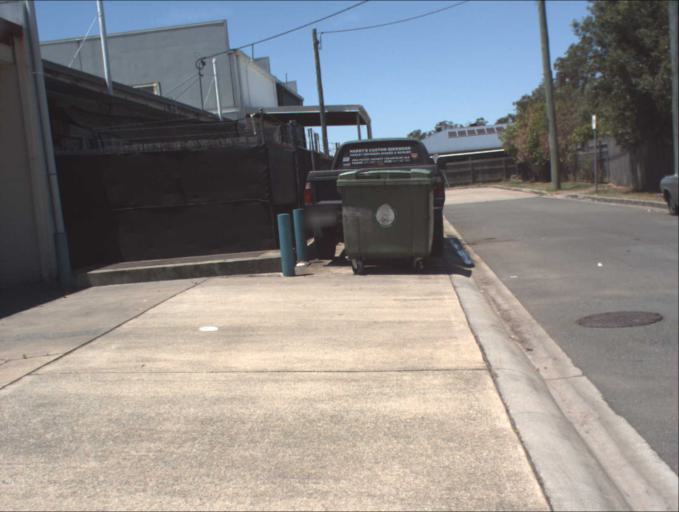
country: AU
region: Queensland
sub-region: Logan
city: Beenleigh
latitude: -27.6811
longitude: 153.1861
